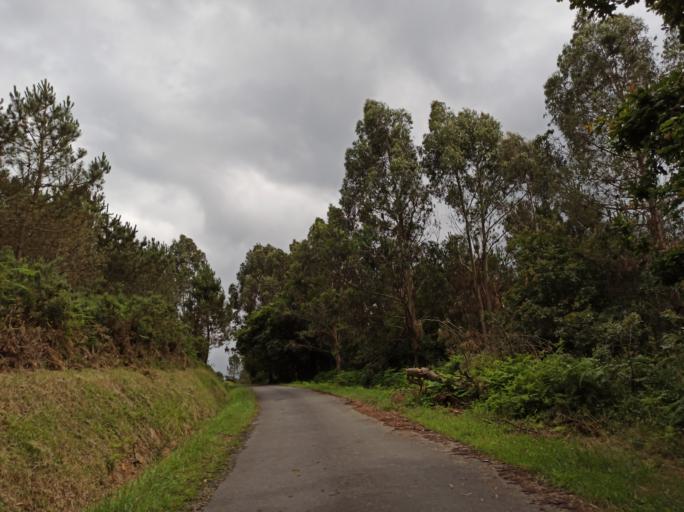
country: ES
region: Galicia
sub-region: Provincia de Pontevedra
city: Silleda
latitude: 42.7693
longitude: -8.1631
